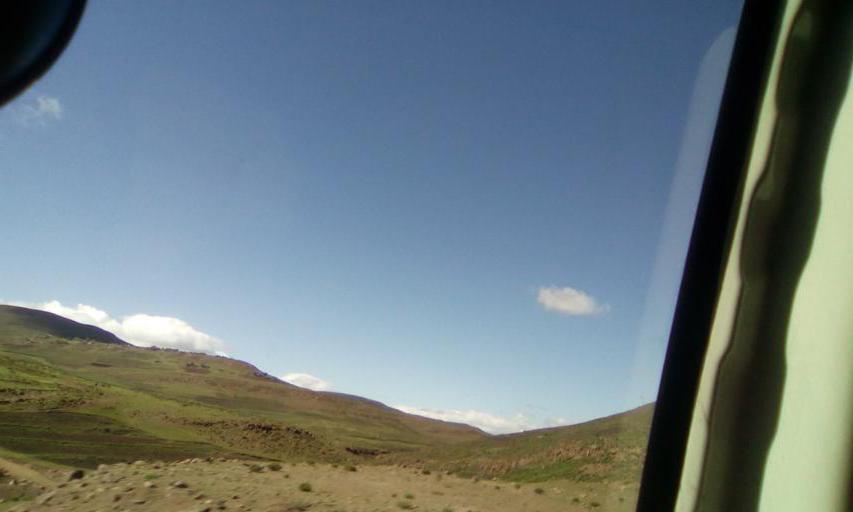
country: LS
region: Maseru
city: Nako
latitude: -29.8844
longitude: 28.0879
